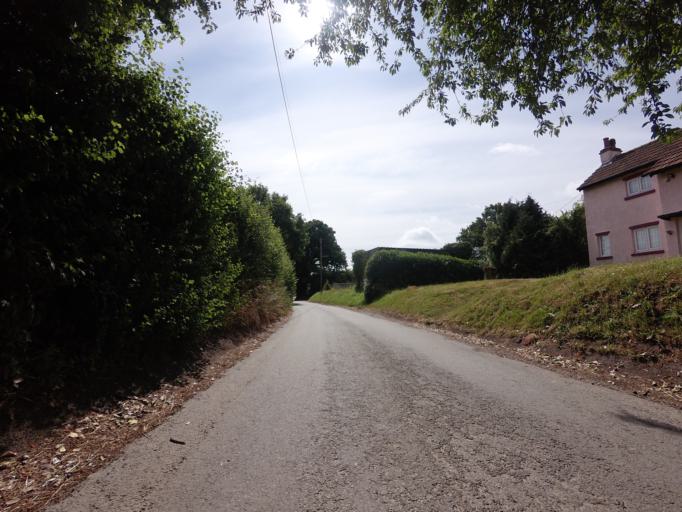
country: GB
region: England
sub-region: Greater London
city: Orpington
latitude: 51.3782
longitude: 0.1345
